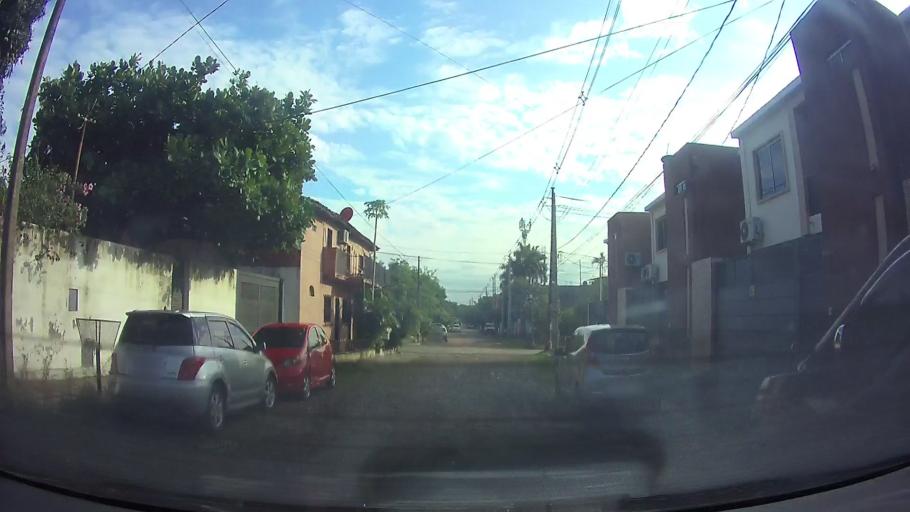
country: PY
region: Central
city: Fernando de la Mora
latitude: -25.2641
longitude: -57.5523
